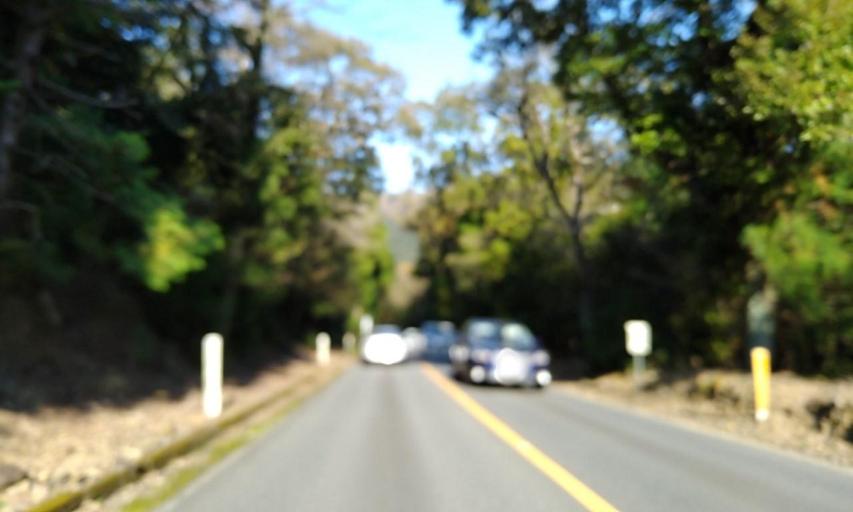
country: JP
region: Mie
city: Ise
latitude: 34.4542
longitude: 136.7421
